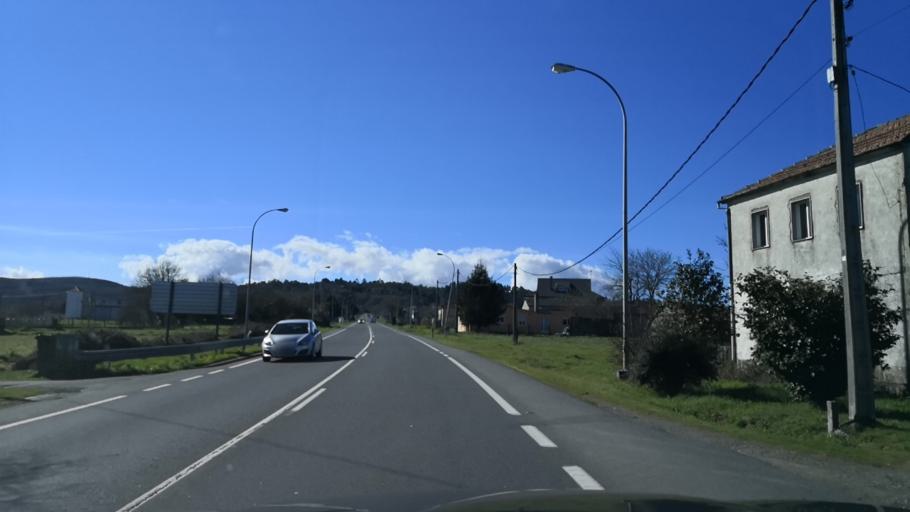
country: ES
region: Galicia
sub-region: Provincia de Pontevedra
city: Silleda
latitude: 42.6870
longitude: -8.2067
